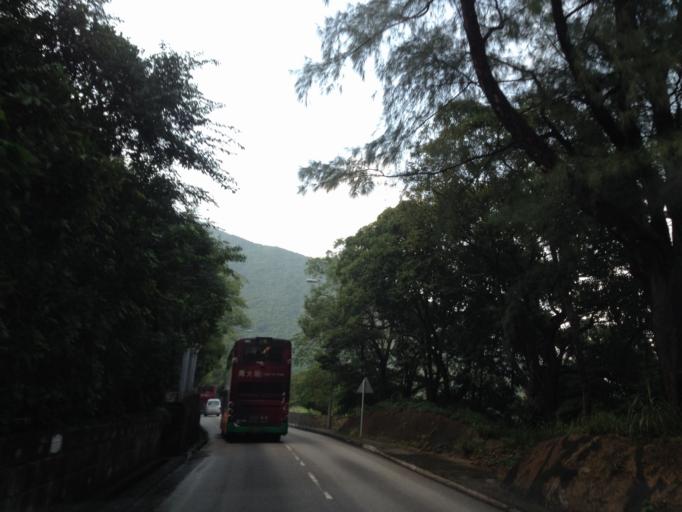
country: HK
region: Wanchai
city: Wan Chai
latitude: 22.2596
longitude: 114.2257
